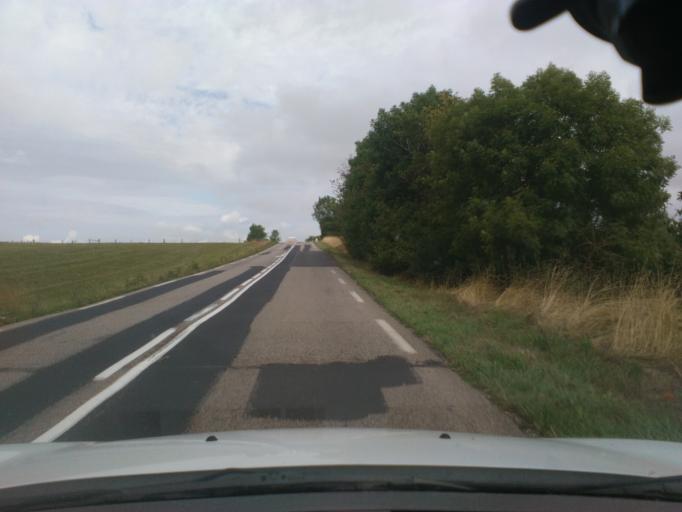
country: FR
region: Lorraine
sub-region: Departement de Meurthe-et-Moselle
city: Vezelise
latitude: 48.4246
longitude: 6.1268
